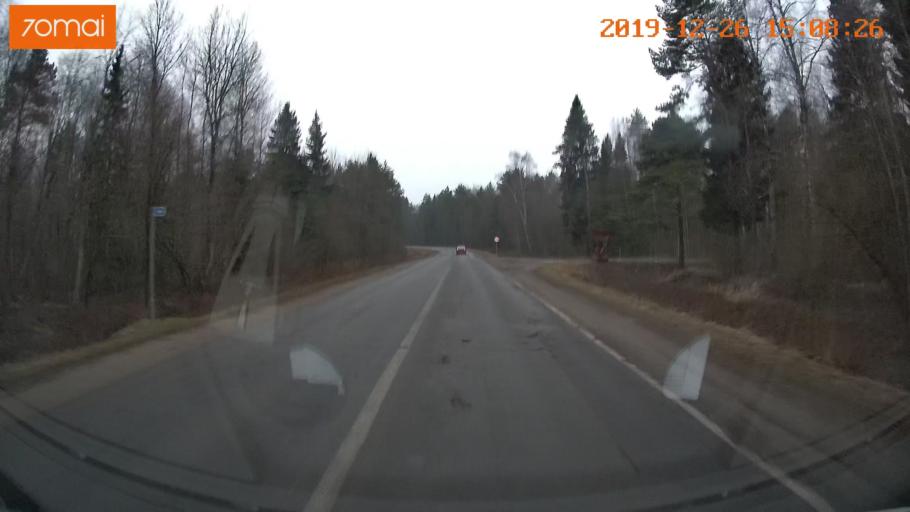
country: RU
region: Jaroslavl
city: Rybinsk
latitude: 58.1597
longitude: 38.8380
